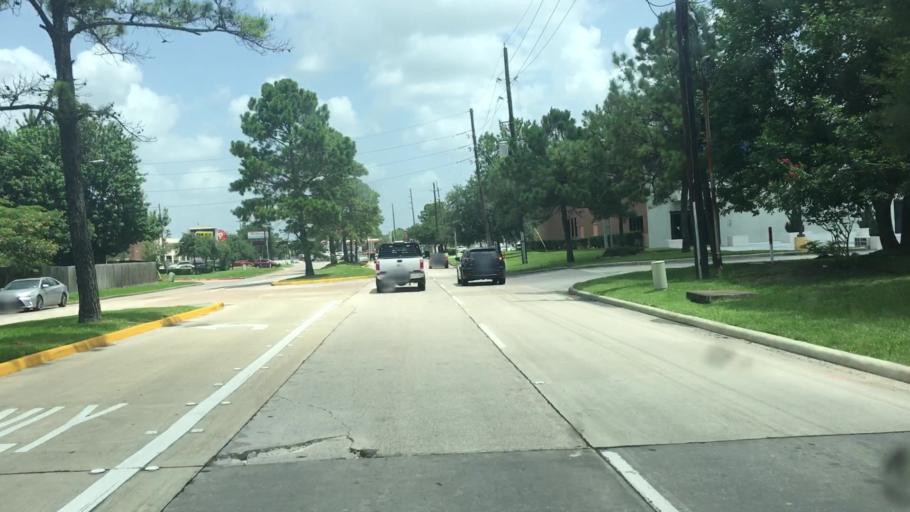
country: US
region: Texas
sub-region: Harris County
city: Atascocita
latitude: 29.9957
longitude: -95.1617
